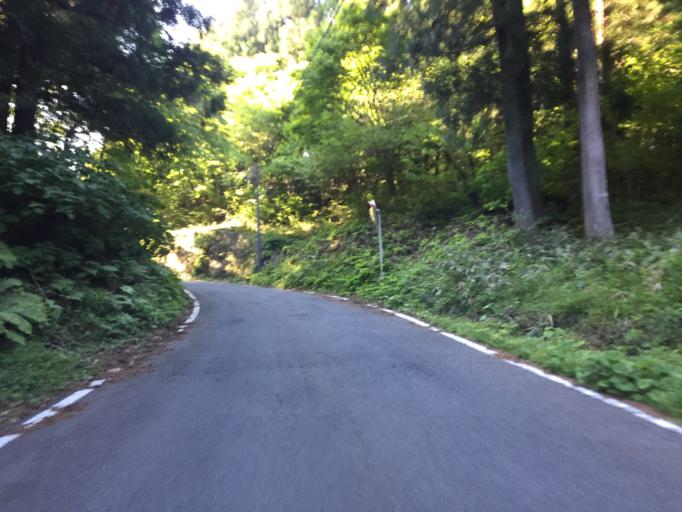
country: JP
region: Ibaraki
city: Kitaibaraki
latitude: 36.9024
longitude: 140.5938
